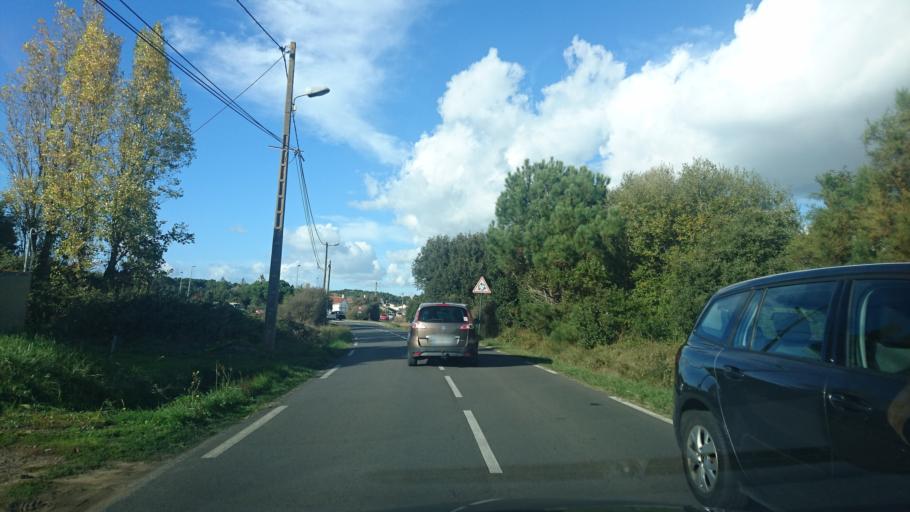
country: FR
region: Pays de la Loire
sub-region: Departement de la Vendee
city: Les Sables-d'Olonne
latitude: 46.5134
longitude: -1.8043
